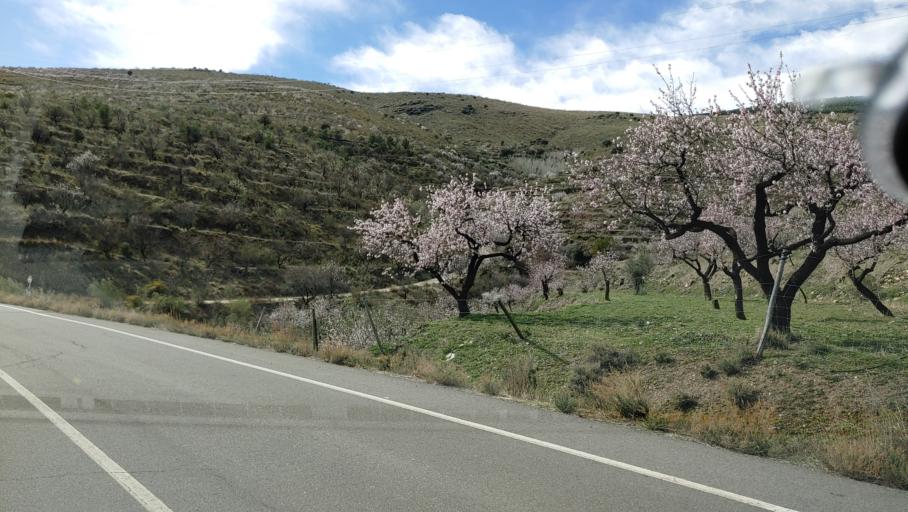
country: ES
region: Andalusia
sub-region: Provincia de Almeria
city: Ohanes
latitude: 37.0615
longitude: -2.7332
